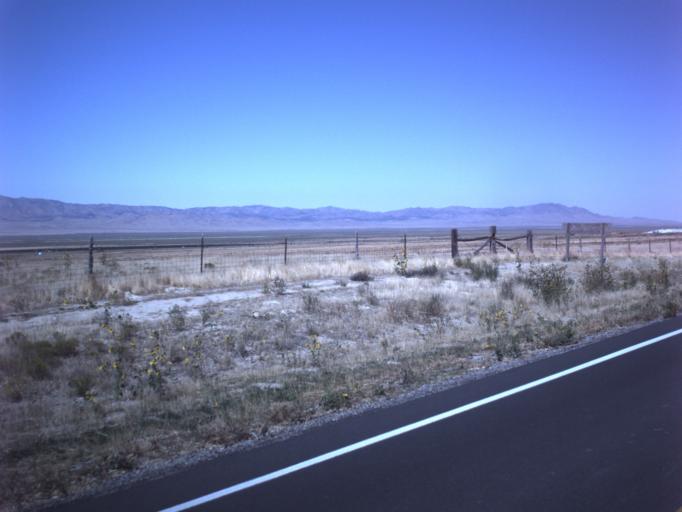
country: US
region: Utah
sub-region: Tooele County
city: Grantsville
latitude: 40.5151
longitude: -112.7477
